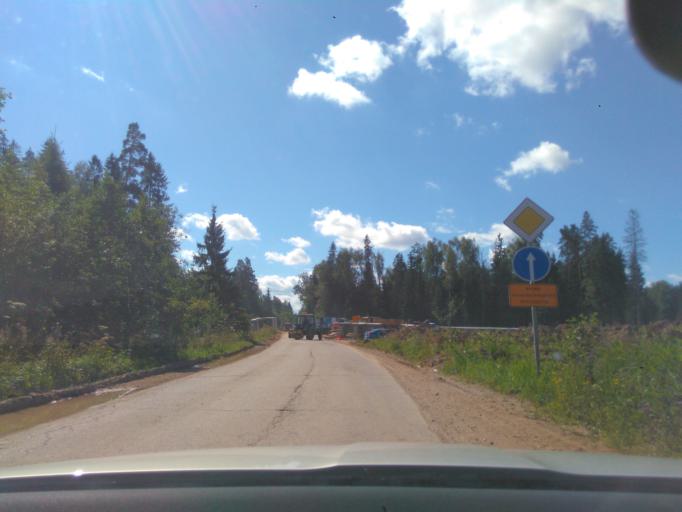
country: RU
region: Moskovskaya
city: Klin
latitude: 56.2095
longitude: 36.8101
